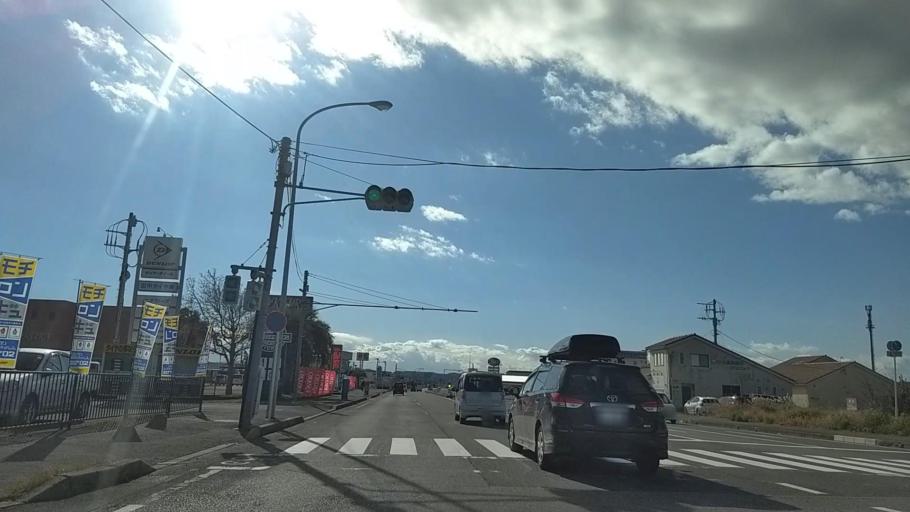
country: JP
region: Chiba
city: Tateyama
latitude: 35.0156
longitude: 139.8718
